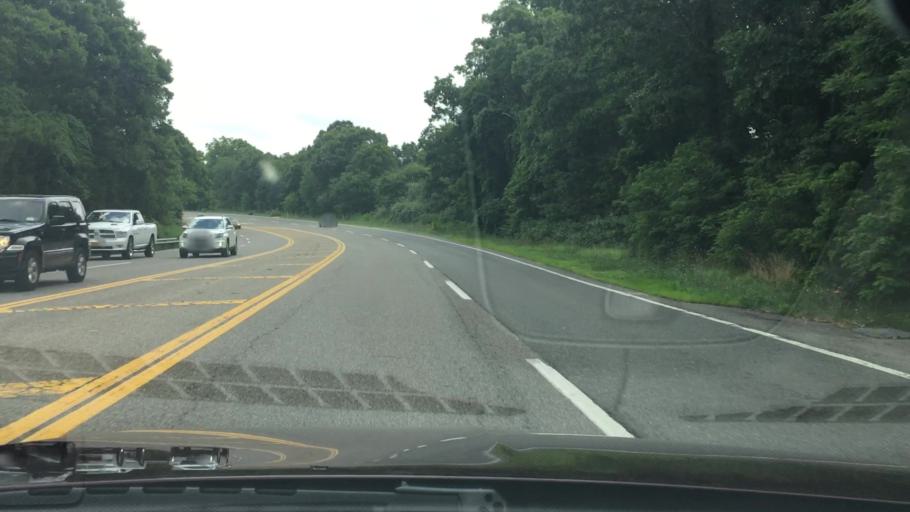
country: US
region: New York
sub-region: Suffolk County
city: Commack
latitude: 40.8096
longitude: -73.2826
